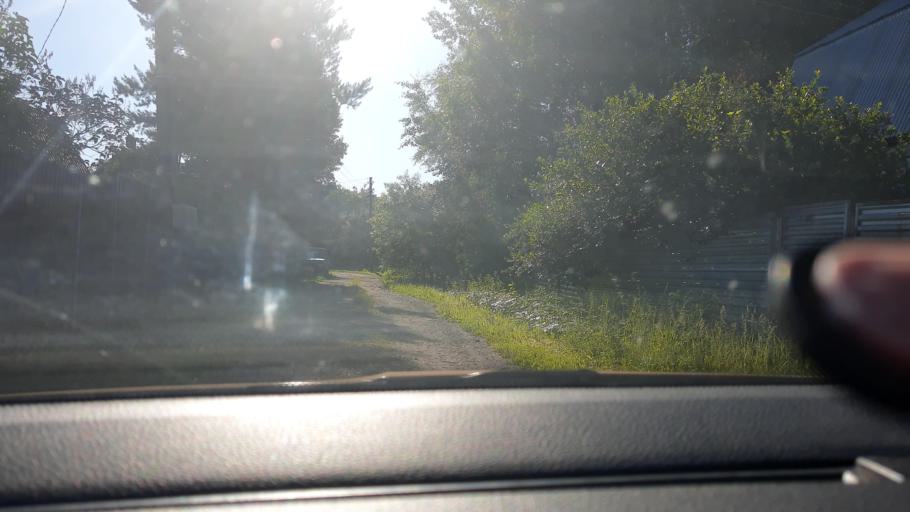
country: RU
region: Moskovskaya
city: Elektrogorsk
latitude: 55.8921
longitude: 38.7252
